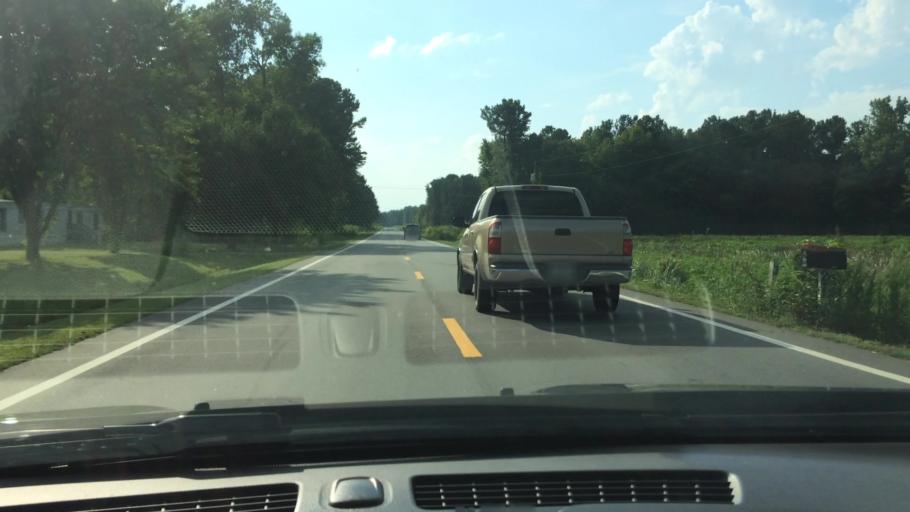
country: US
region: North Carolina
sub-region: Craven County
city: Vanceboro
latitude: 35.4324
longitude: -77.1324
